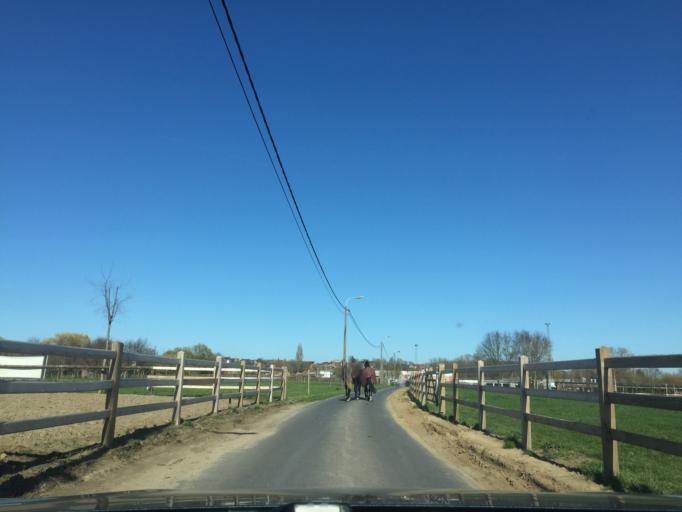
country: BE
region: Flanders
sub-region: Provincie West-Vlaanderen
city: Hooglede
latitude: 50.9739
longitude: 3.0669
